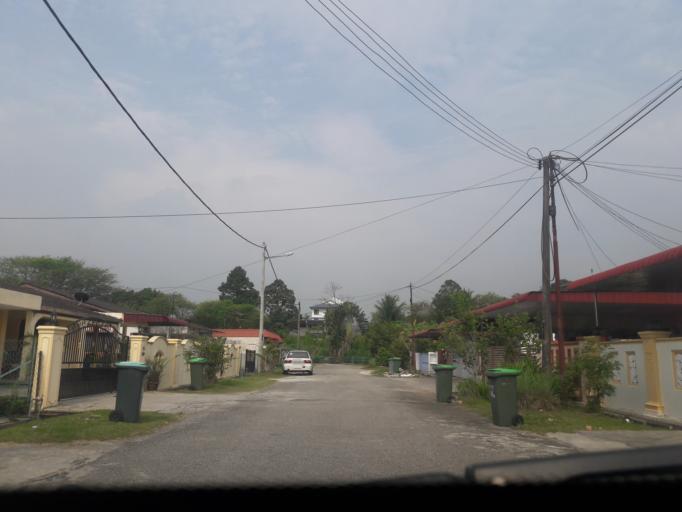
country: MY
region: Kedah
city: Kulim
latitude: 5.3566
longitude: 100.5396
